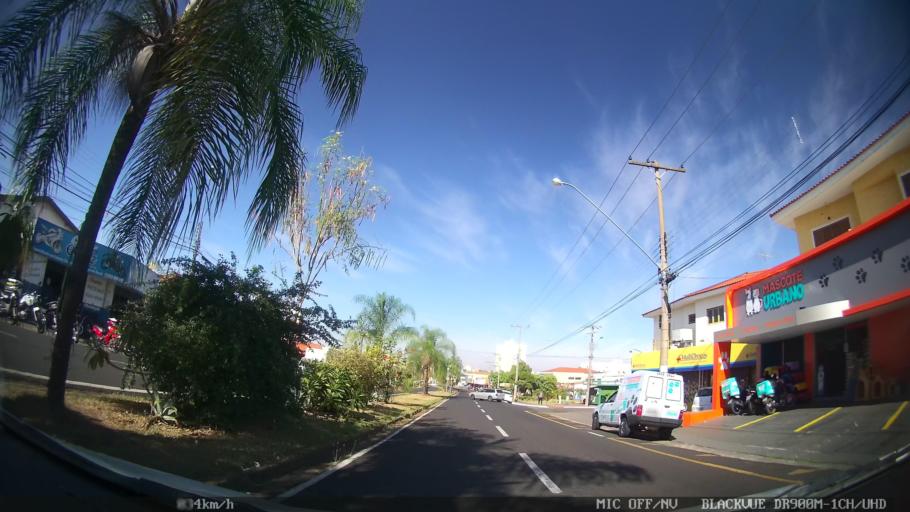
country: BR
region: Sao Paulo
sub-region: Sao Jose Do Rio Preto
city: Sao Jose do Rio Preto
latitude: -20.7824
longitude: -49.3685
